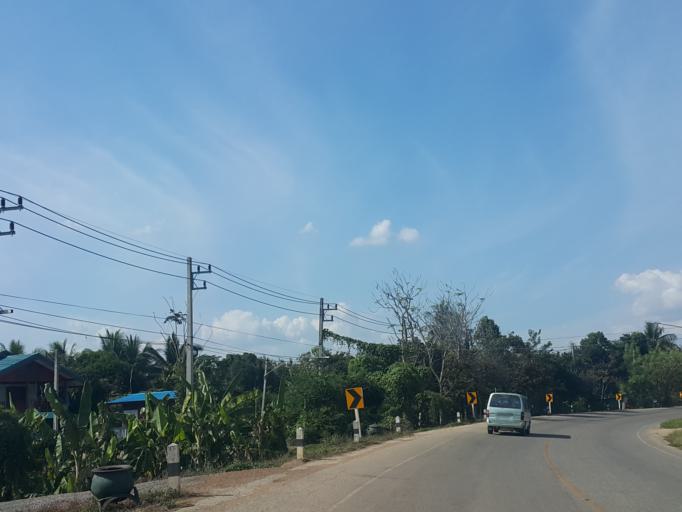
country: TH
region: Sukhothai
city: Sawankhalok
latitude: 17.2580
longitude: 99.8373
